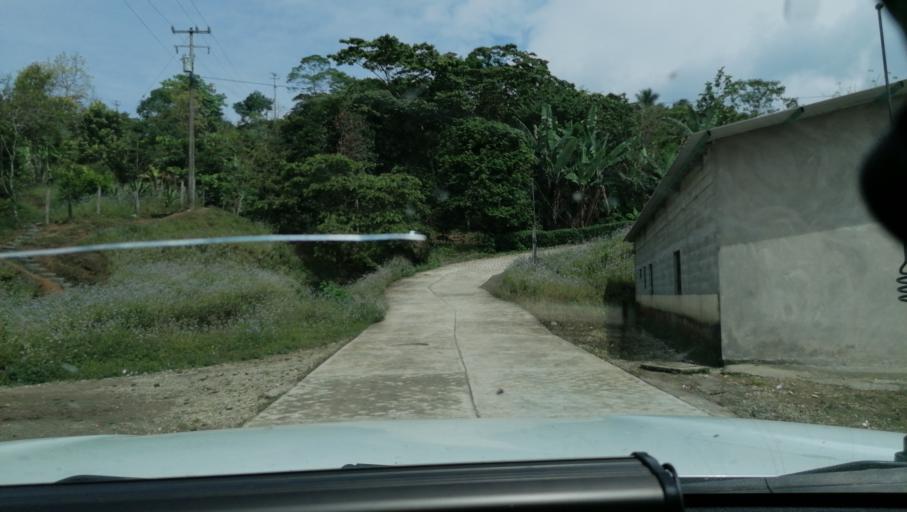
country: MX
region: Chiapas
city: Ocotepec
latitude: 17.3079
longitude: -93.1820
